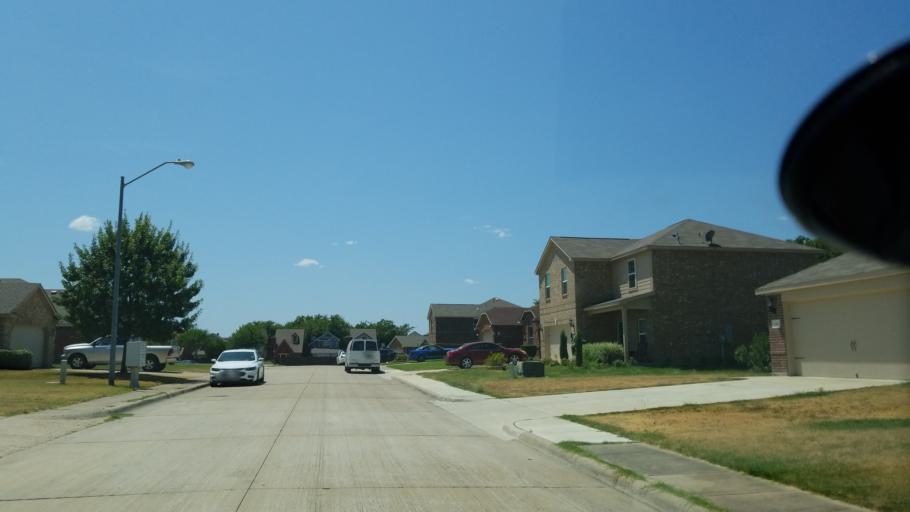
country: US
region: Texas
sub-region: Dallas County
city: Duncanville
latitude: 32.6444
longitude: -96.8849
